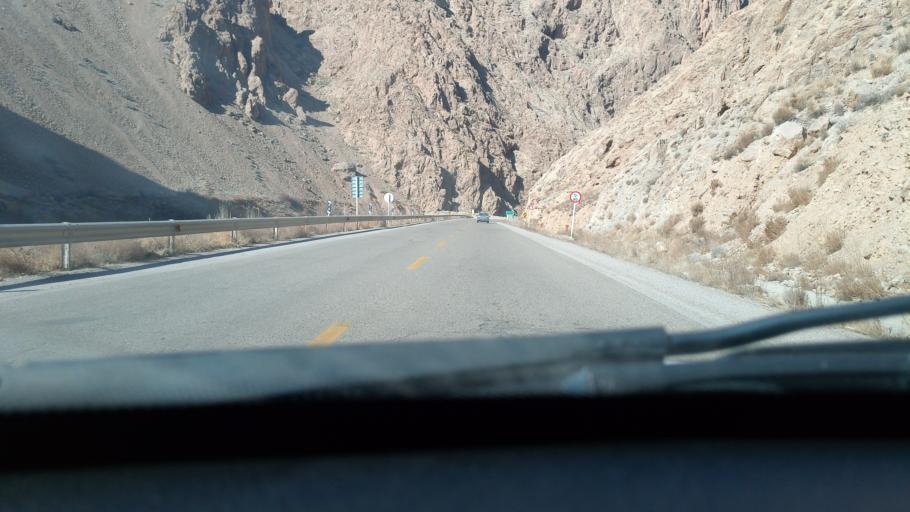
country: IR
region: Khorasan-e Shomali
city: Esfarayen
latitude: 37.1769
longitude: 57.4158
